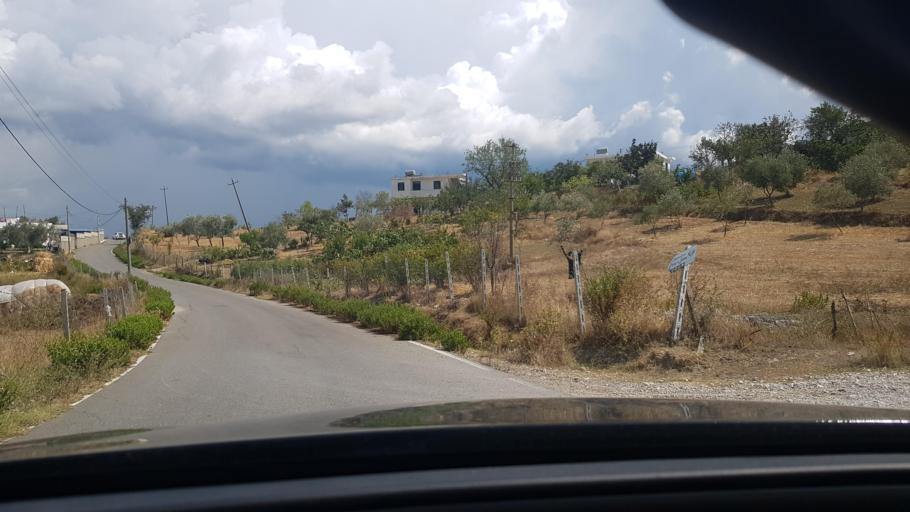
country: AL
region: Durres
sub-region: Rrethi i Durresit
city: Rrashbull
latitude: 41.2920
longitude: 19.5359
